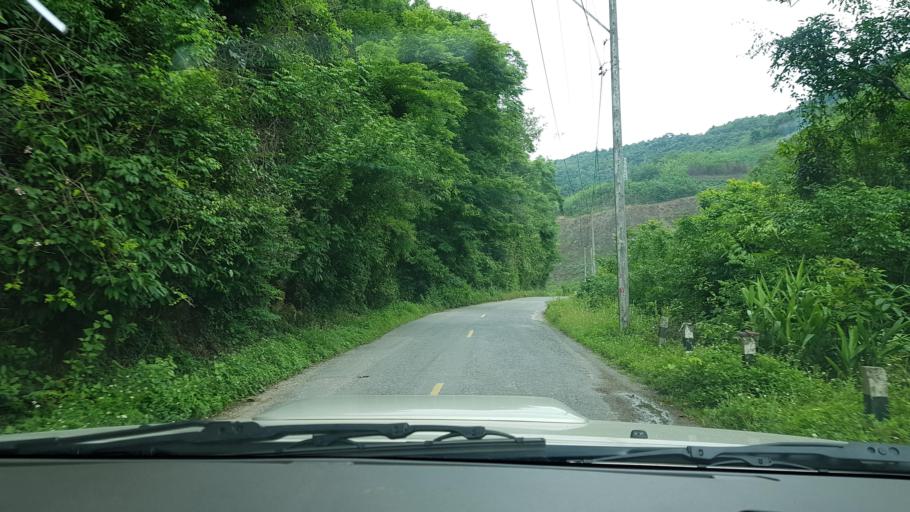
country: LA
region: Oudomxai
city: Muang La
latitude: 20.8762
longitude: 102.1465
